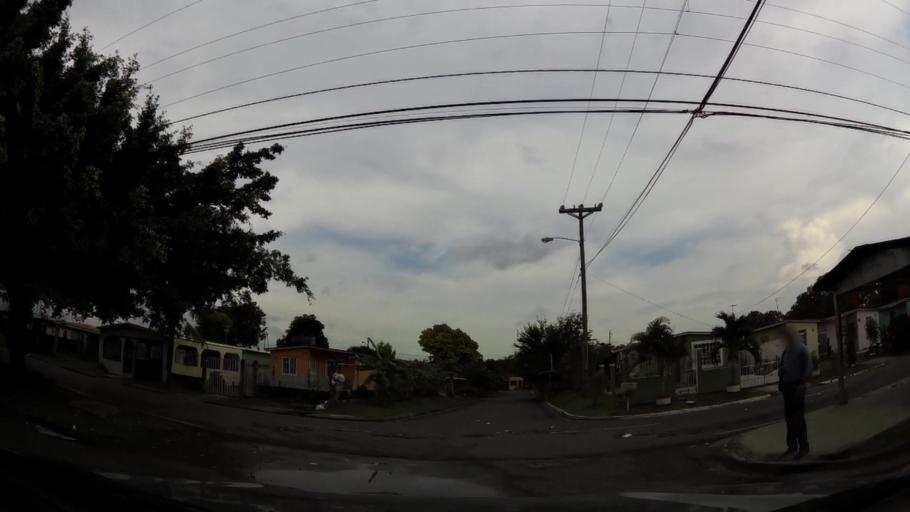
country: PA
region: Panama
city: Cabra Numero Uno
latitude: 9.0882
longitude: -79.3435
